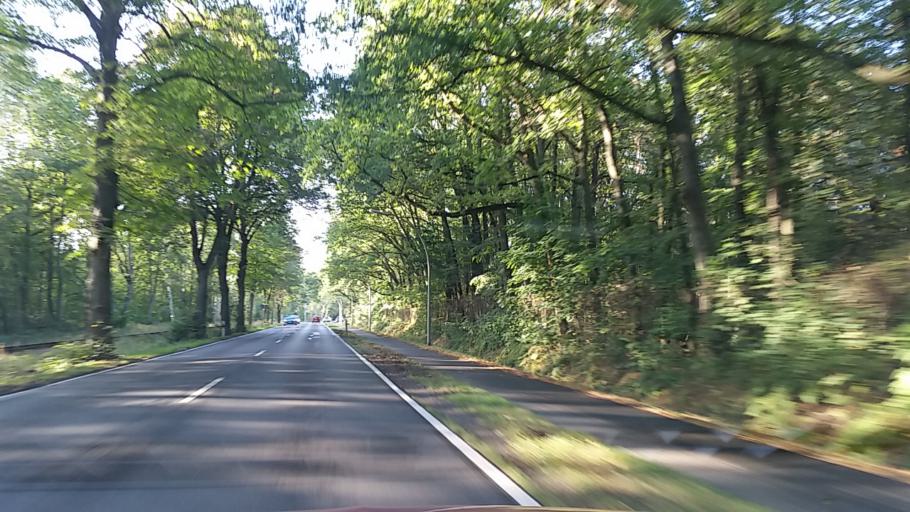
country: DE
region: Lower Saxony
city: Braunschweig
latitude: 52.3057
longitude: 10.5432
